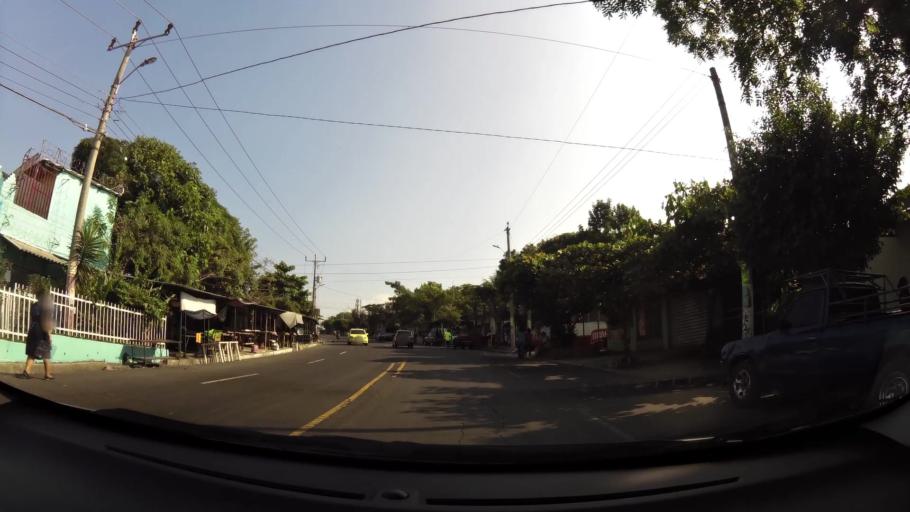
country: SV
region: San Salvador
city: Ilopango
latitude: 13.7141
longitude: -89.1072
